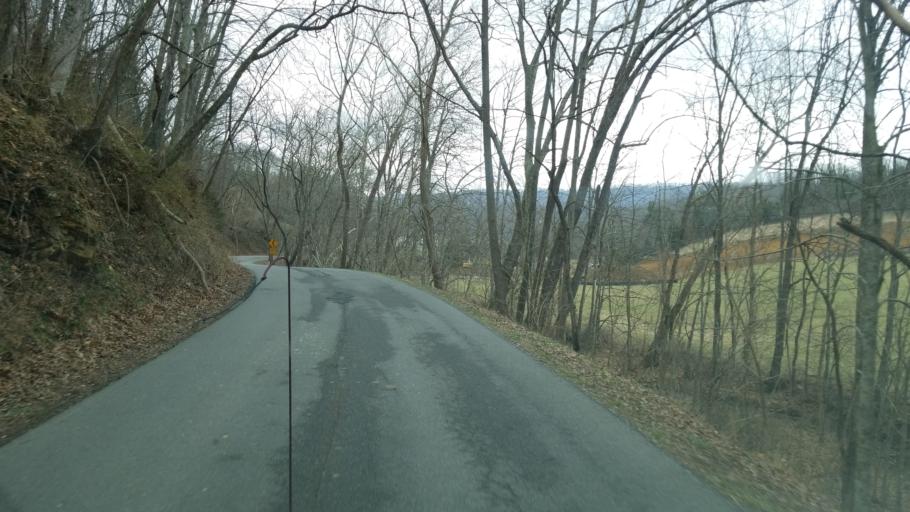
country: US
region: Virginia
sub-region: Giles County
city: Pembroke
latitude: 37.2476
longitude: -80.6825
